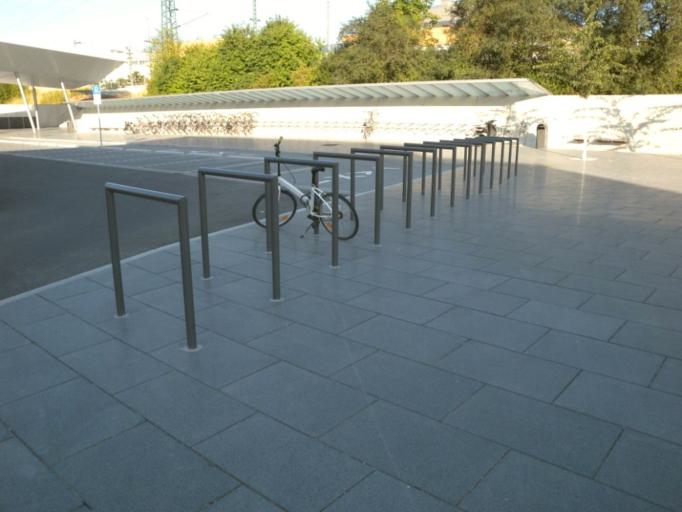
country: DE
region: Baden-Wuerttemberg
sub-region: Regierungsbezirk Stuttgart
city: Boeblingen
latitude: 48.6882
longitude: 9.0035
